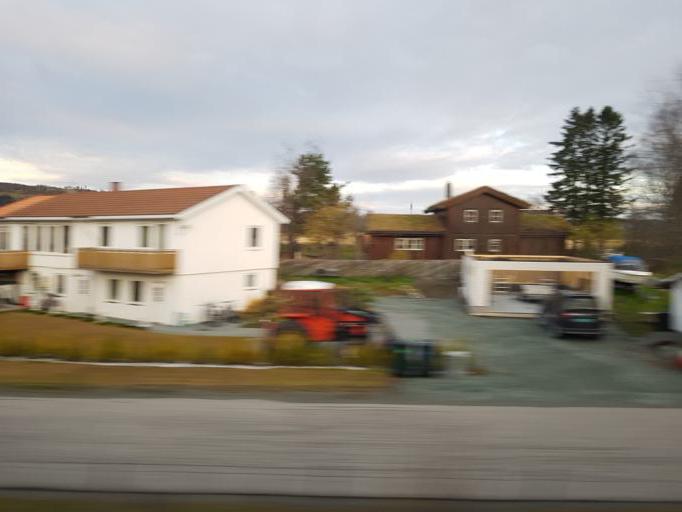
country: NO
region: Sor-Trondelag
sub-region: Melhus
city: Melhus
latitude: 63.2951
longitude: 10.2910
